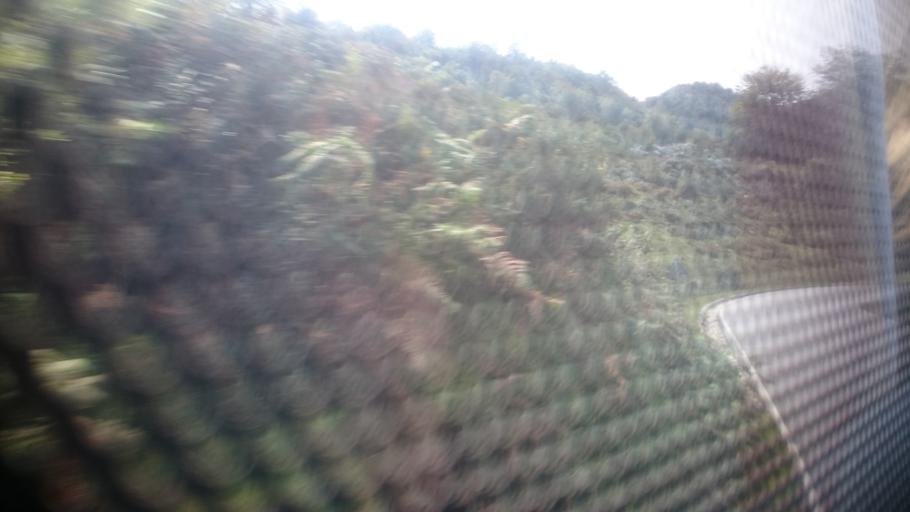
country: ES
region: Asturias
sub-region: Province of Asturias
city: Amieva
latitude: 43.2894
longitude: -5.0136
